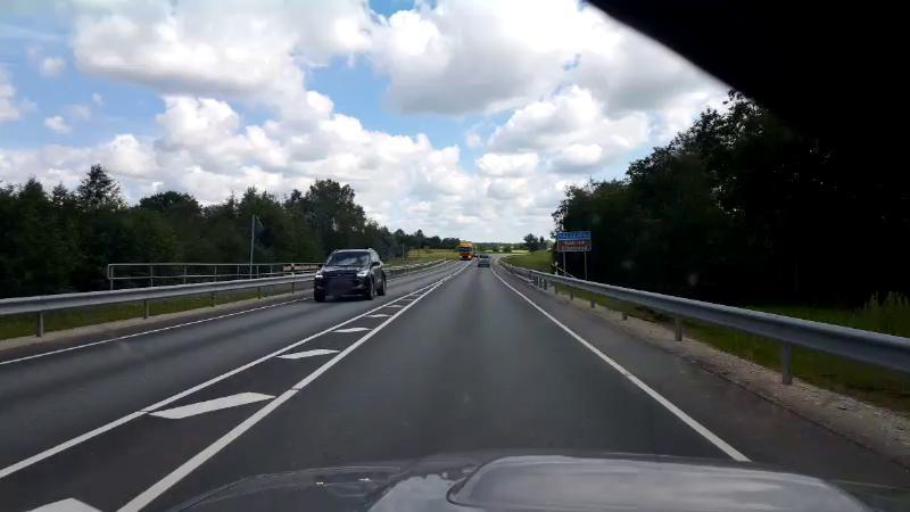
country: EE
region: Laeaene-Virumaa
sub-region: Tapa vald
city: Tapa
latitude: 59.2596
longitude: 26.0032
